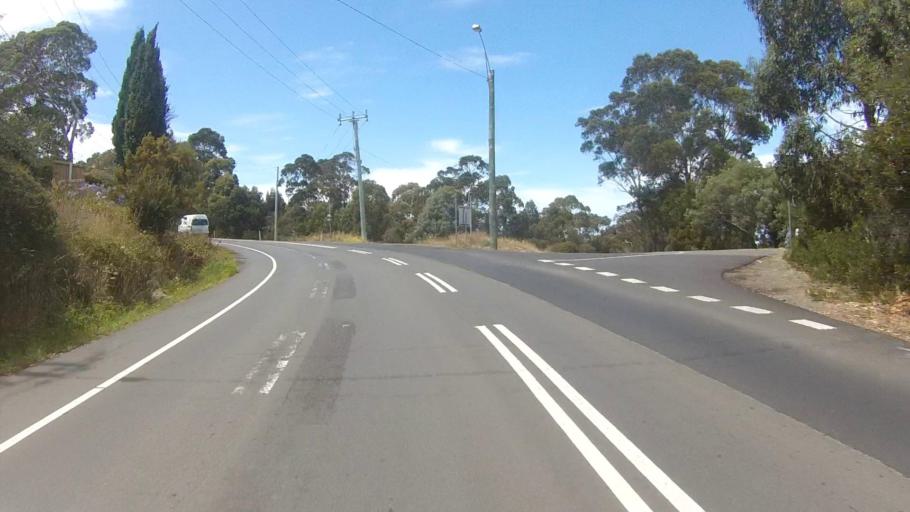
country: AU
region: Tasmania
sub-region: Kingborough
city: Kingston Beach
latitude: -42.9716
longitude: 147.3266
